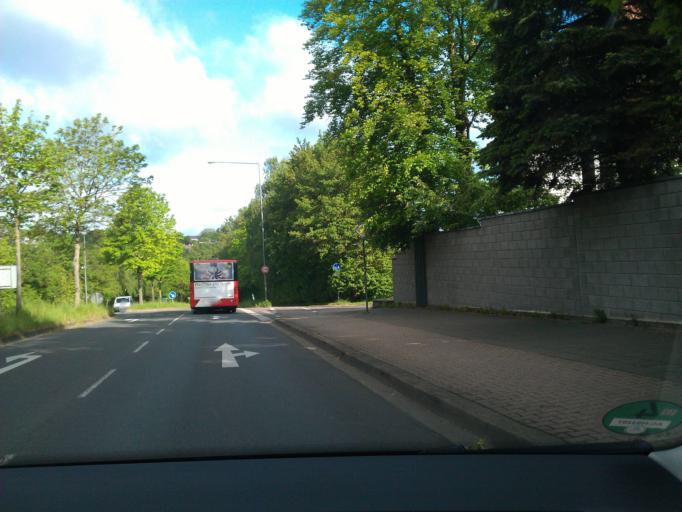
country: DE
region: North Rhine-Westphalia
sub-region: Regierungsbezirk Koln
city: Aachen
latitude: 50.7613
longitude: 6.0641
